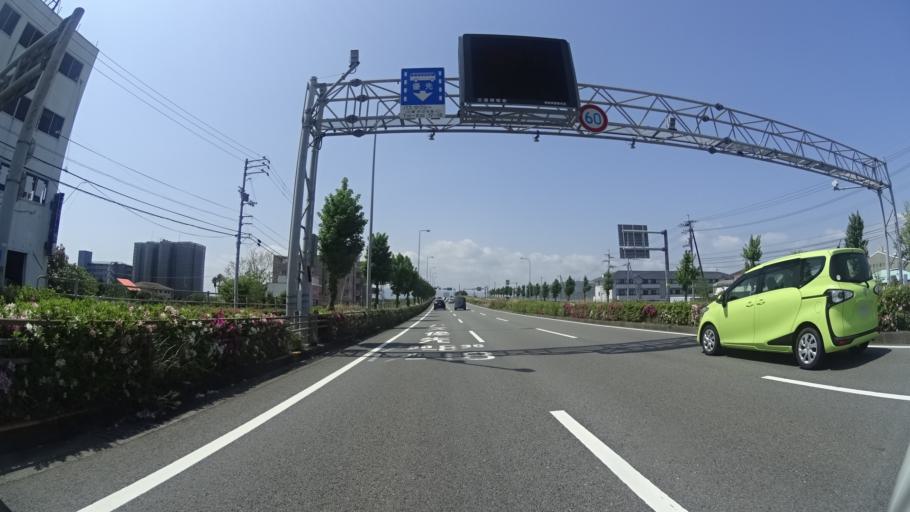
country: JP
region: Tokushima
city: Tokushima-shi
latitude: 34.0964
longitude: 134.5727
